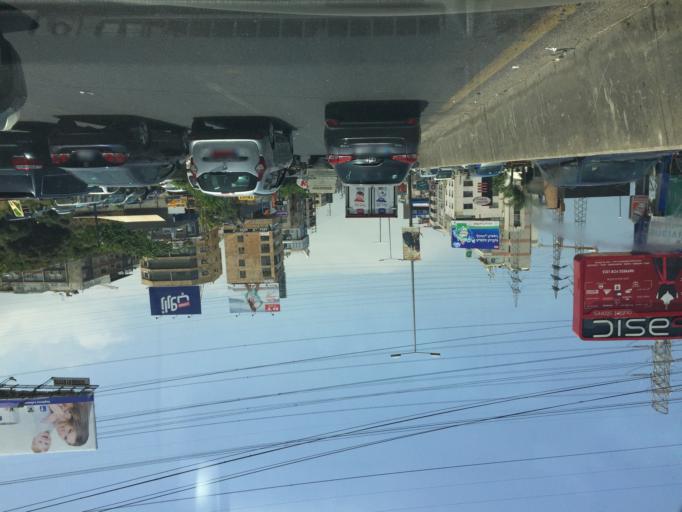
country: LB
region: Mont-Liban
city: Djounie
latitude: 33.9678
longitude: 35.6077
